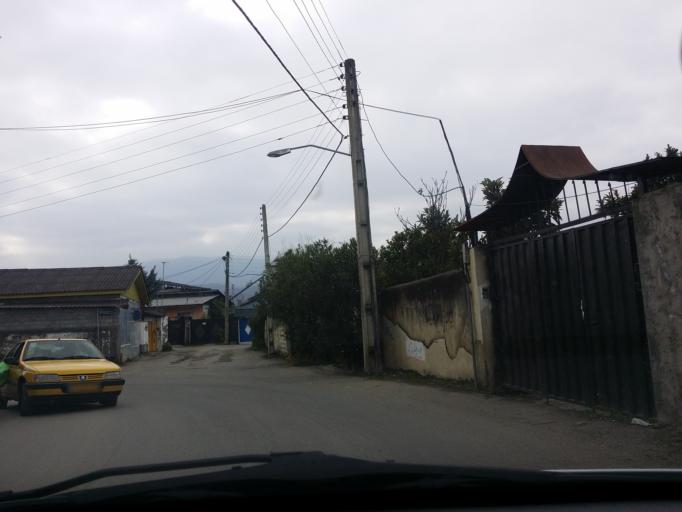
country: IR
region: Mazandaran
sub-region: Nowshahr
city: Nowshahr
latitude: 36.6565
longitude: 51.4768
